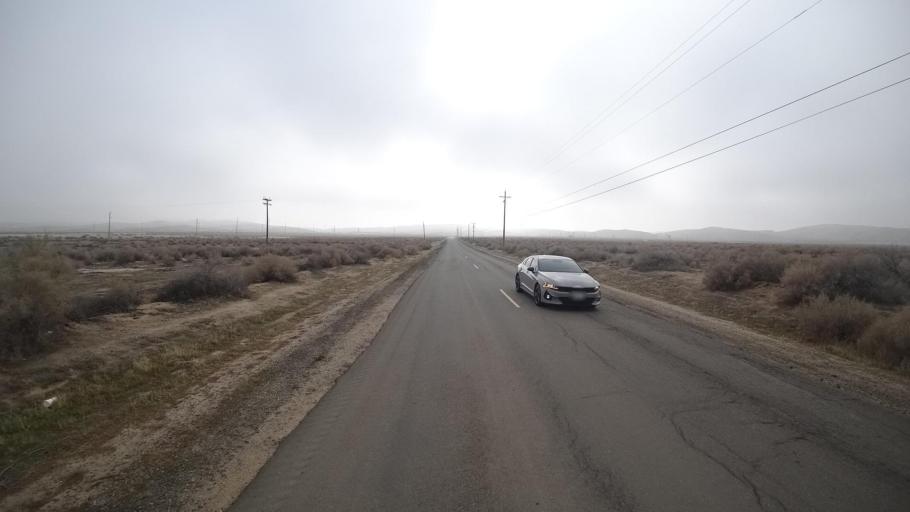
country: US
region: California
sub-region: Kern County
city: Ford City
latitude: 35.1848
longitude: -119.4290
